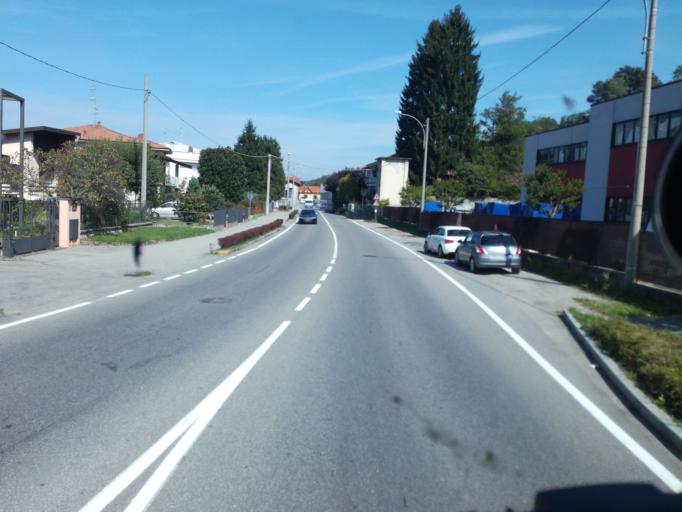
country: IT
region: Lombardy
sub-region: Provincia di Varese
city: Castronno
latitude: 45.7559
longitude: 8.8109
